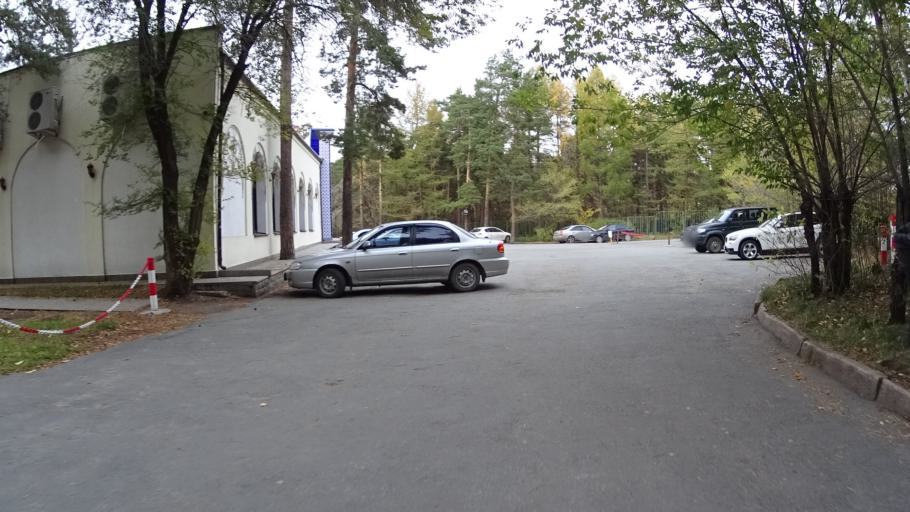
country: RU
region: Chelyabinsk
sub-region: Gorod Chelyabinsk
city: Chelyabinsk
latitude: 55.1653
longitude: 61.3662
